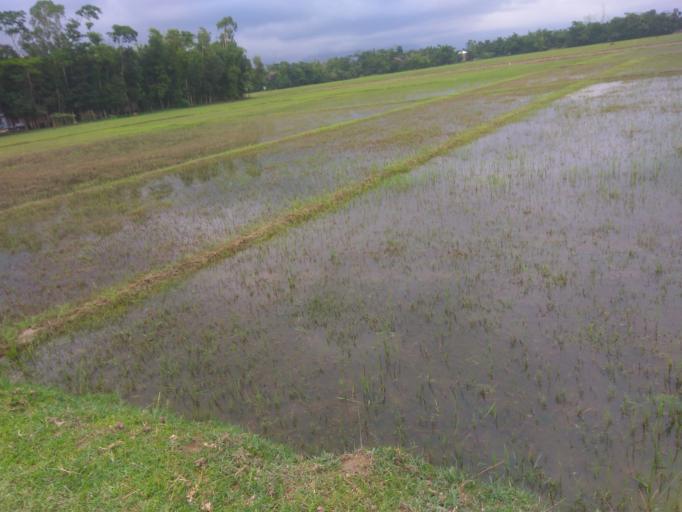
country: IN
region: Assam
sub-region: Karimganj
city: Karimganj
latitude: 24.9913
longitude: 92.3838
